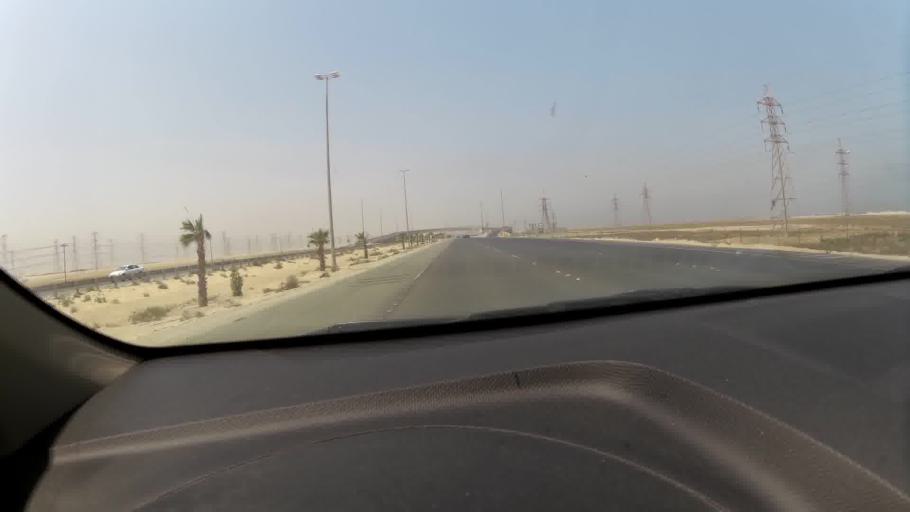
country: KW
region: Al Ahmadi
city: Al Fahahil
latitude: 28.8217
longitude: 48.2595
